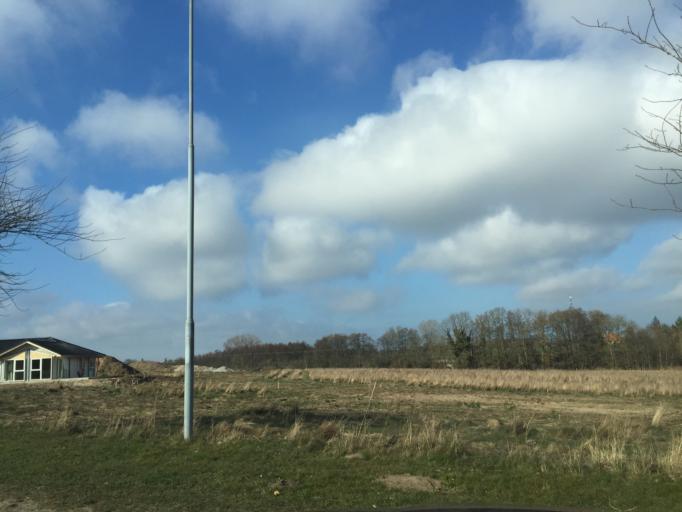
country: DK
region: South Denmark
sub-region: Odense Kommune
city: Neder Holluf
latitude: 55.3853
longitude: 10.4628
